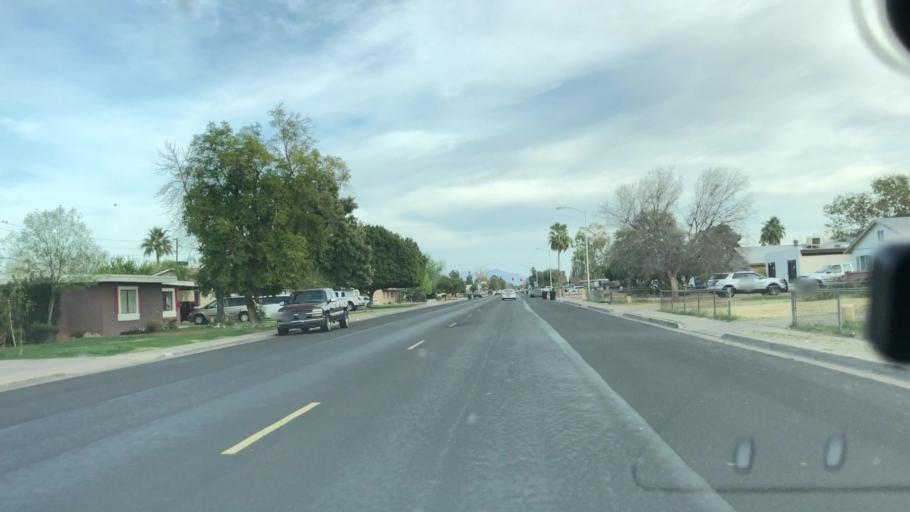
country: US
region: Arizona
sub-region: Maricopa County
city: Mesa
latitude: 33.4008
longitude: -111.7919
